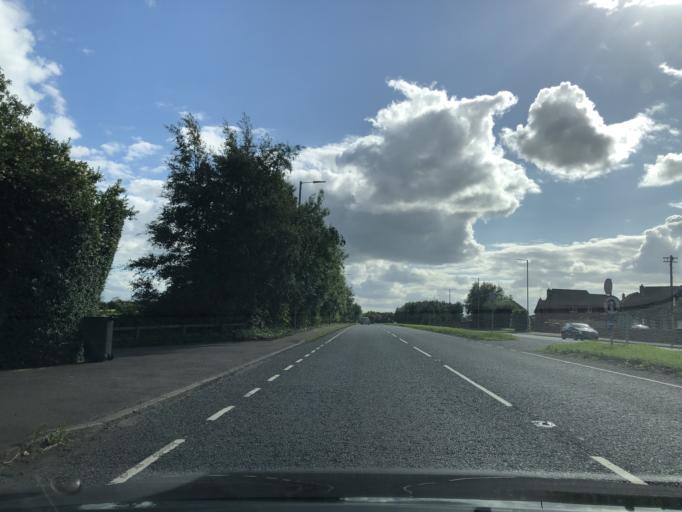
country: GB
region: Northern Ireland
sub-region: Ards District
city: Comber
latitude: 54.5540
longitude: -5.7240
